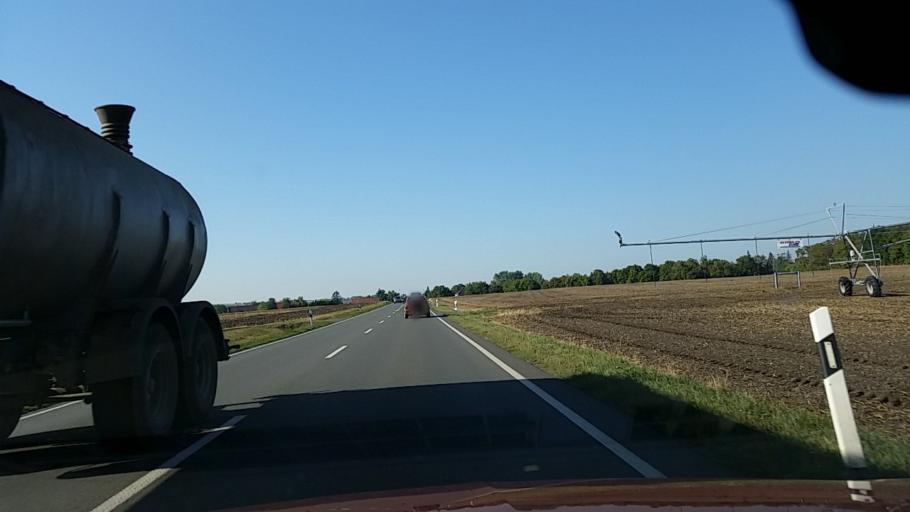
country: DE
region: Thuringia
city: Sprotau
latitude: 51.1684
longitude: 11.1905
